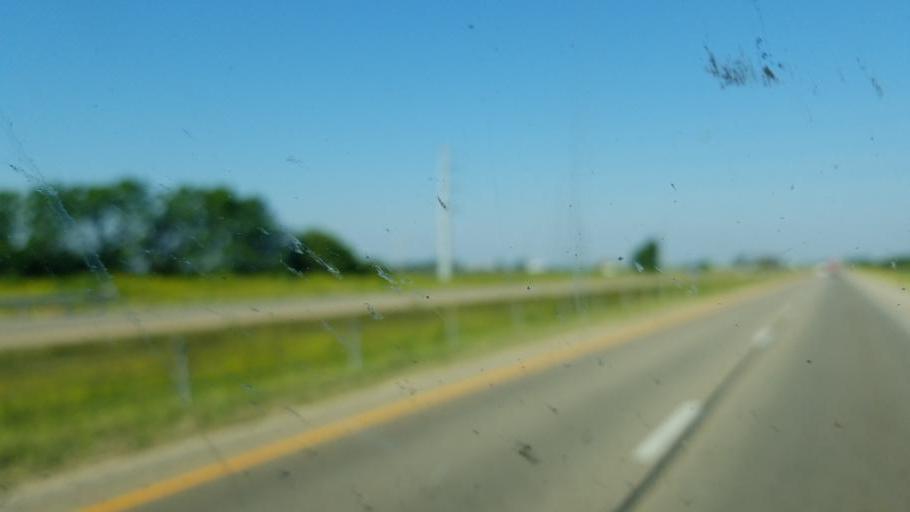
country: US
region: Illinois
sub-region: LaSalle County
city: Ottawa
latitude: 41.3685
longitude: -88.8944
